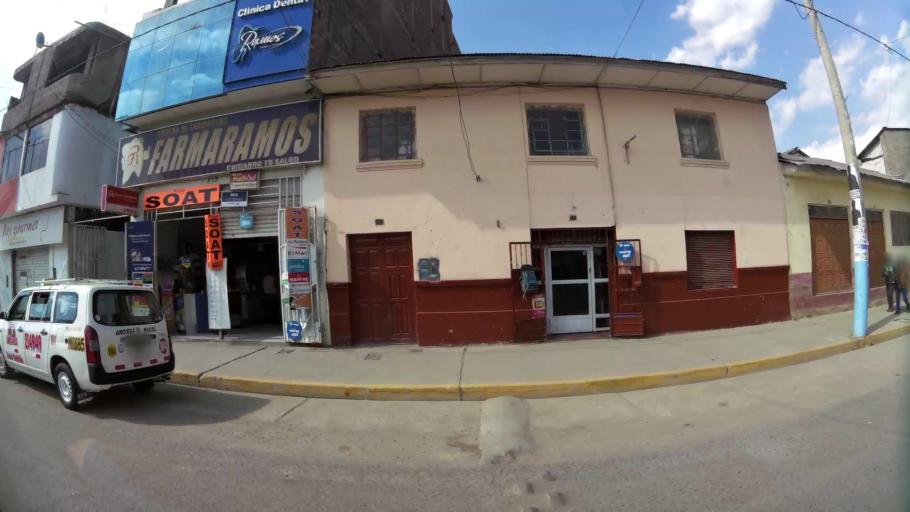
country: PE
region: Junin
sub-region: Provincia de Huancayo
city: Huancayo
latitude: -12.0834
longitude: -75.2011
